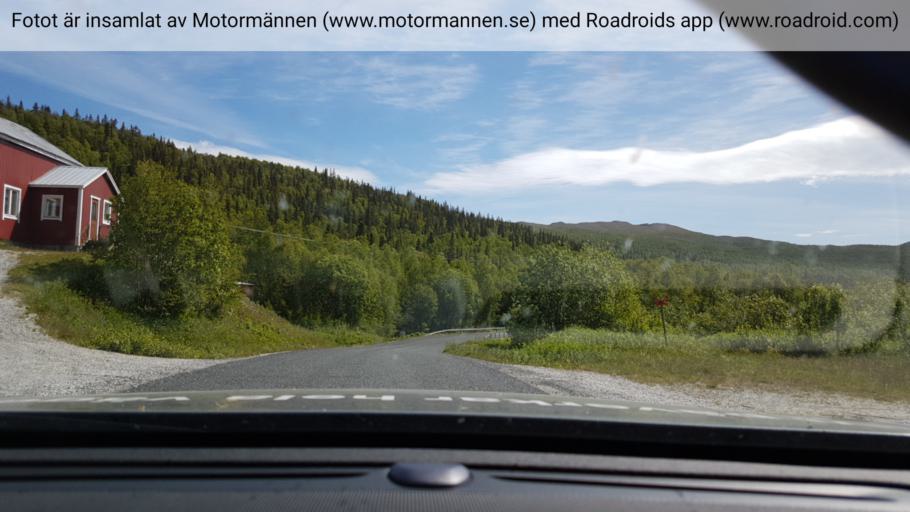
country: SE
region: Vaesterbotten
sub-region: Vilhelmina Kommun
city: Sjoberg
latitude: 65.3217
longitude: 15.2816
